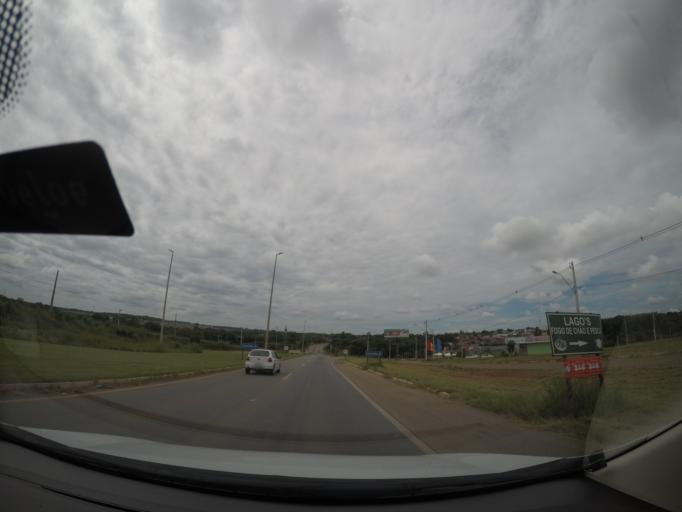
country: BR
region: Goias
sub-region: Goianira
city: Goianira
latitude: -16.4912
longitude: -49.4244
